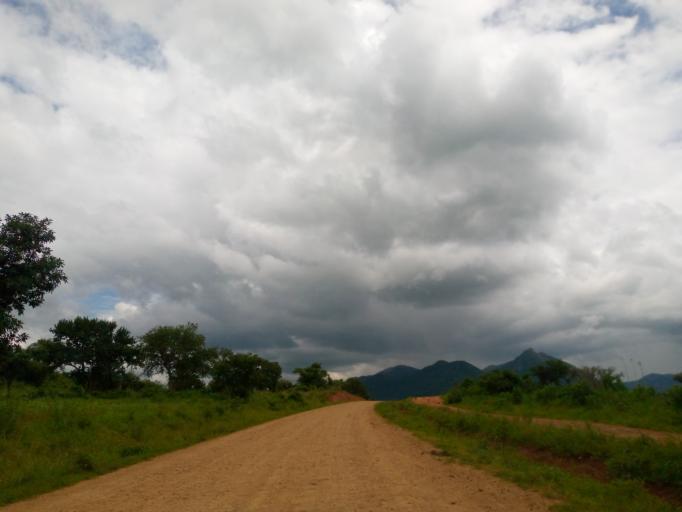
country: ET
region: Oromiya
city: Mendi
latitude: 10.1916
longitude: 35.0934
